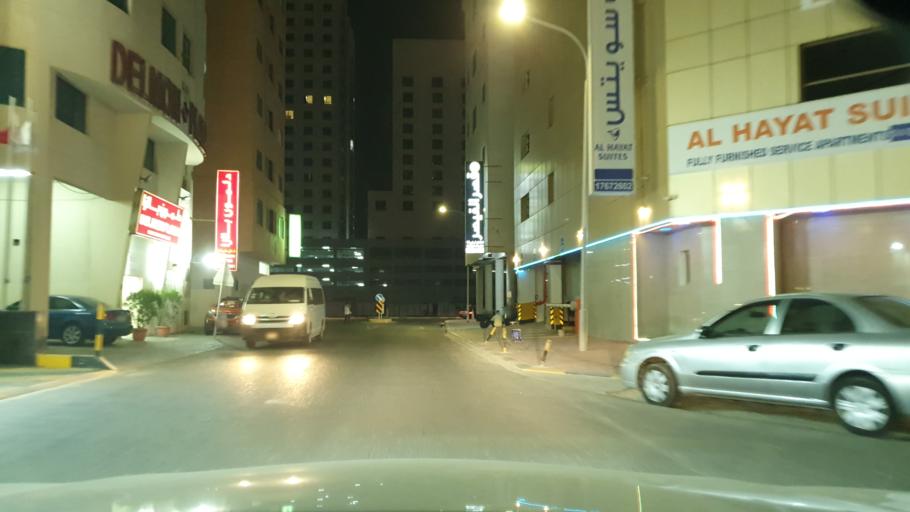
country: BH
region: Manama
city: Manama
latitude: 26.2184
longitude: 50.6051
